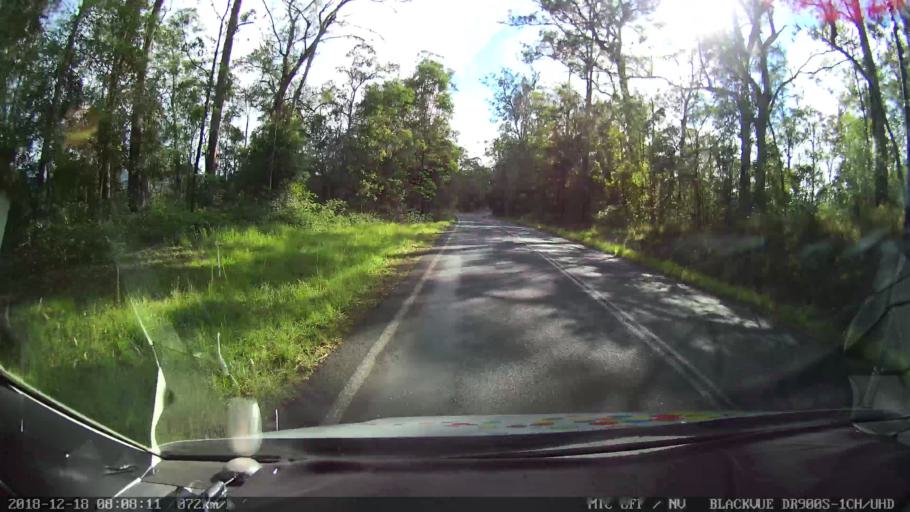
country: AU
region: New South Wales
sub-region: Kyogle
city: Kyogle
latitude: -28.3823
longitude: 152.6491
